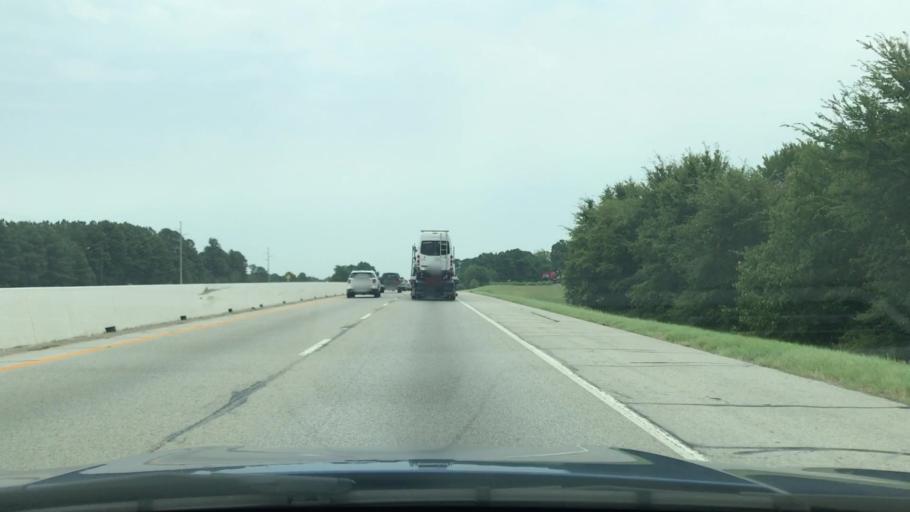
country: US
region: Texas
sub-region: Smith County
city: Hideaway
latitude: 32.4782
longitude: -95.4855
